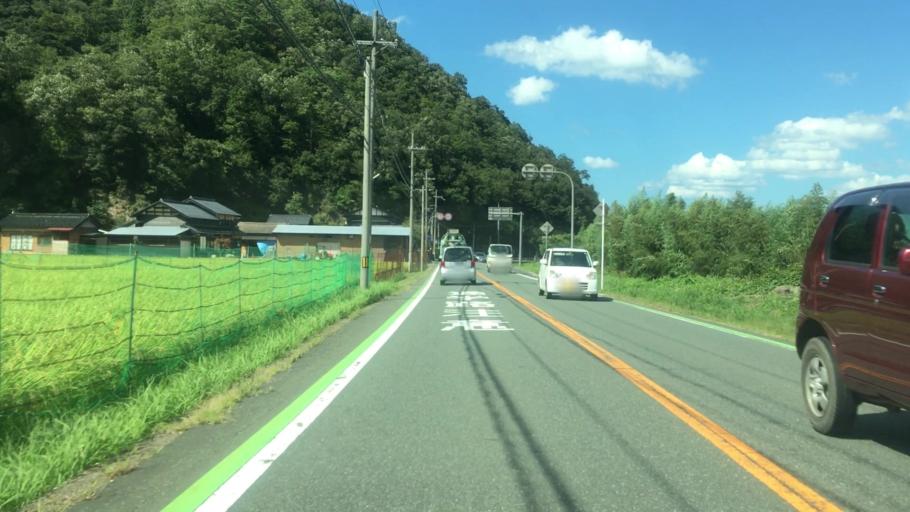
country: JP
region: Kyoto
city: Miyazu
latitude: 35.5841
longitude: 135.0355
